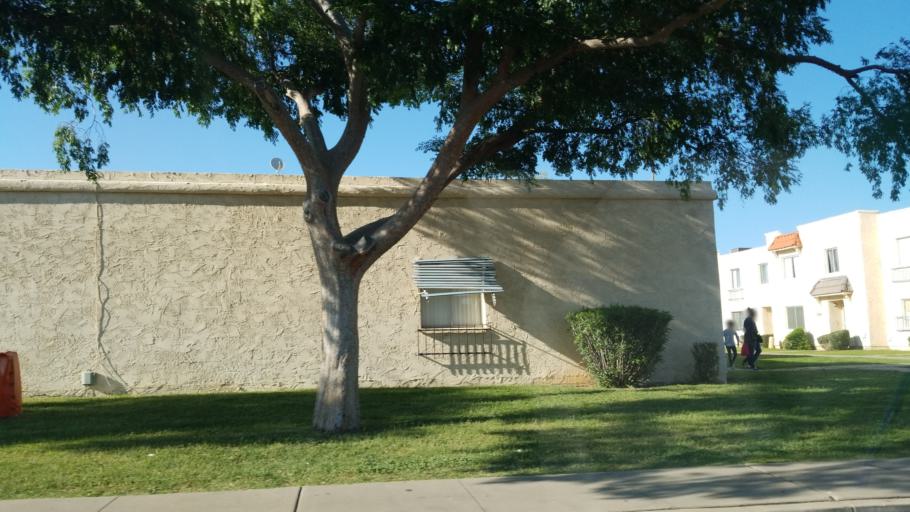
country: US
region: Arizona
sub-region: Maricopa County
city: Glendale
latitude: 33.5203
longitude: -112.1534
